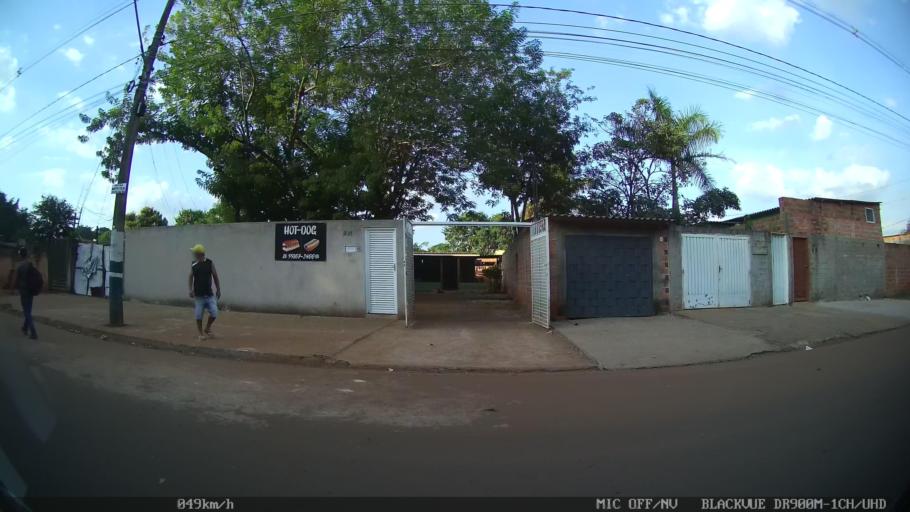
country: BR
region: Sao Paulo
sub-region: Ribeirao Preto
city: Ribeirao Preto
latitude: -21.1169
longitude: -47.8035
